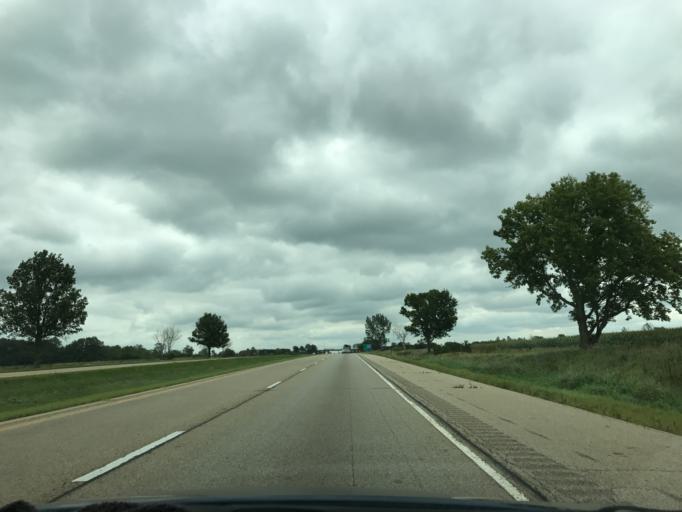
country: US
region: Illinois
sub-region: Bureau County
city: Ladd
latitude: 41.3696
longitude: -89.2307
